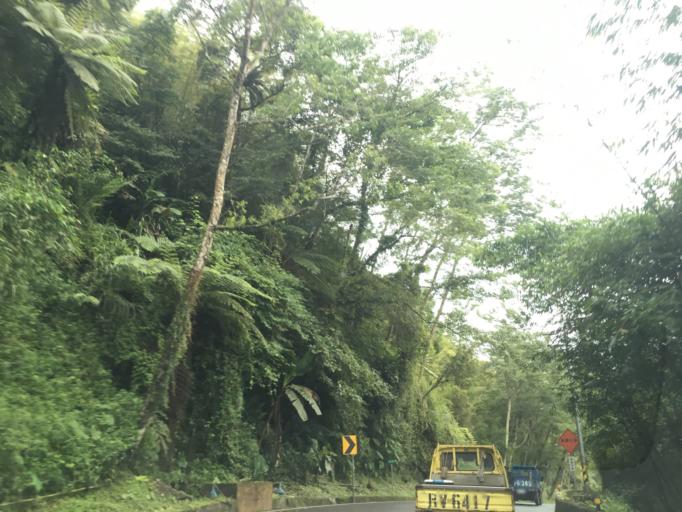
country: TW
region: Taiwan
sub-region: Chiayi
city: Jiayi Shi
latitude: 23.4611
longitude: 120.6881
